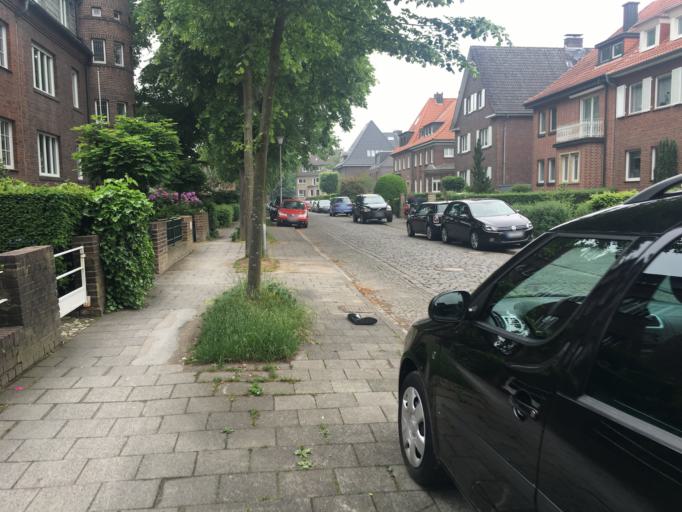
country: DE
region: North Rhine-Westphalia
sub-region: Regierungsbezirk Munster
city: Muenster
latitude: 51.9625
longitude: 7.6536
